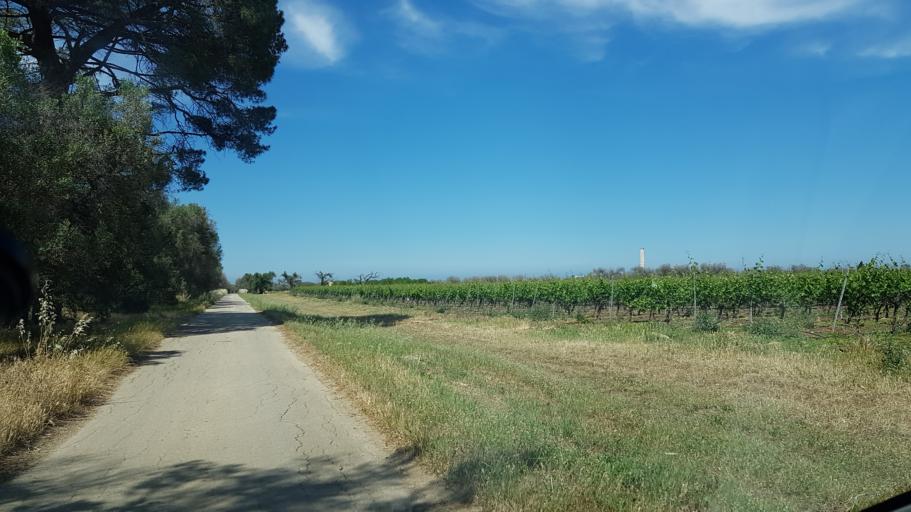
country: IT
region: Apulia
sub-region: Provincia di Brindisi
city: San Pietro Vernotico
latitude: 40.5383
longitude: 17.9970
